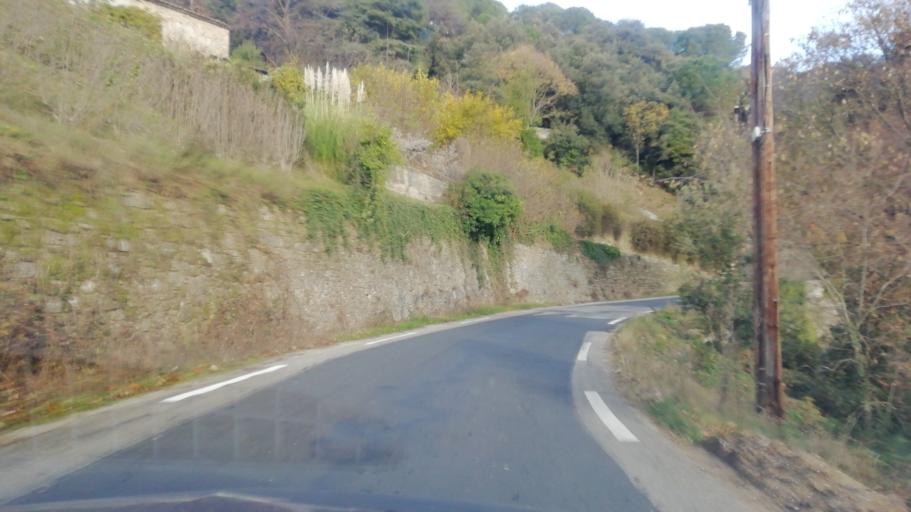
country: FR
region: Languedoc-Roussillon
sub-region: Departement du Gard
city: Lasalle
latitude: 44.0162
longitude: 3.8485
